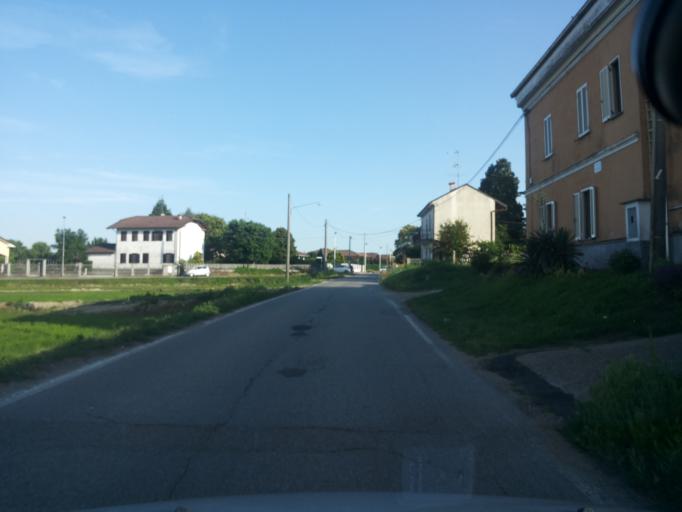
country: IT
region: Piedmont
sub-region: Provincia di Vercelli
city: Pezzana
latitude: 45.2643
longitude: 8.4778
